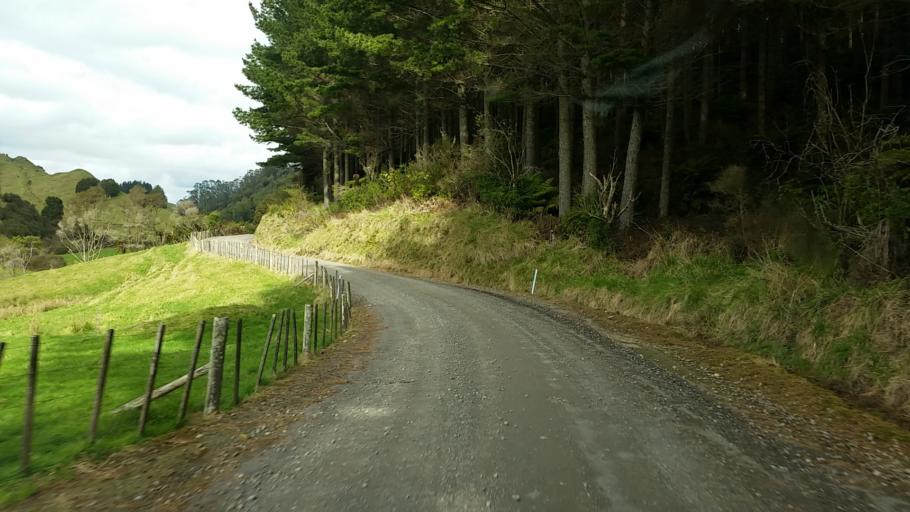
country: NZ
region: Taranaki
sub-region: New Plymouth District
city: Waitara
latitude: -39.1557
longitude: 174.5606
